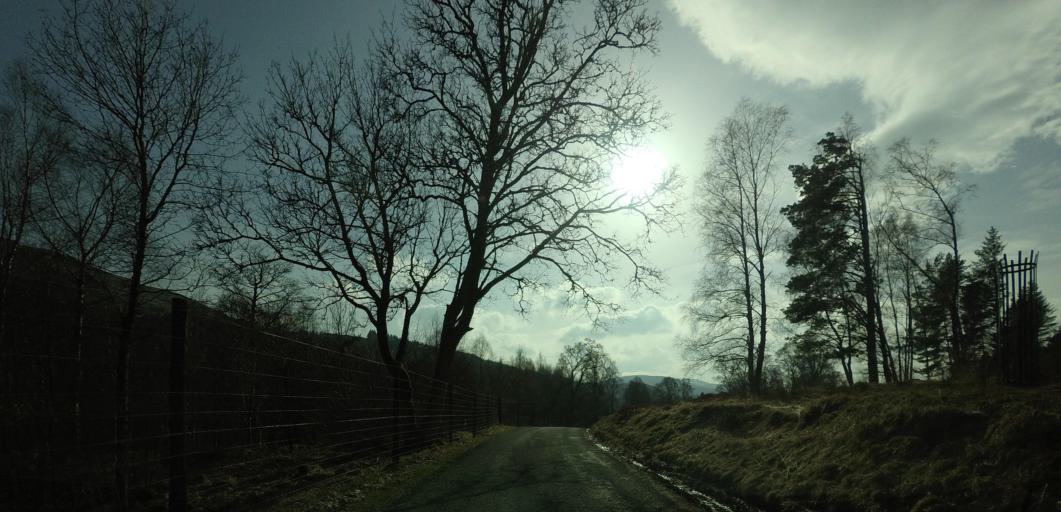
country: GB
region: Scotland
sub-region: Stirling
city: Callander
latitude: 56.5961
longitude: -4.3040
